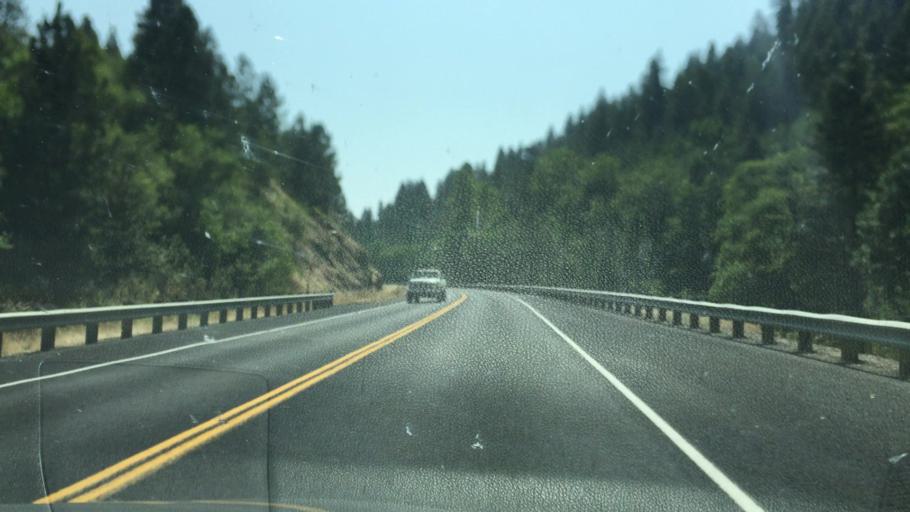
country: US
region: Idaho
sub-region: Nez Perce County
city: Lapwai
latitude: 46.3567
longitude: -116.6287
